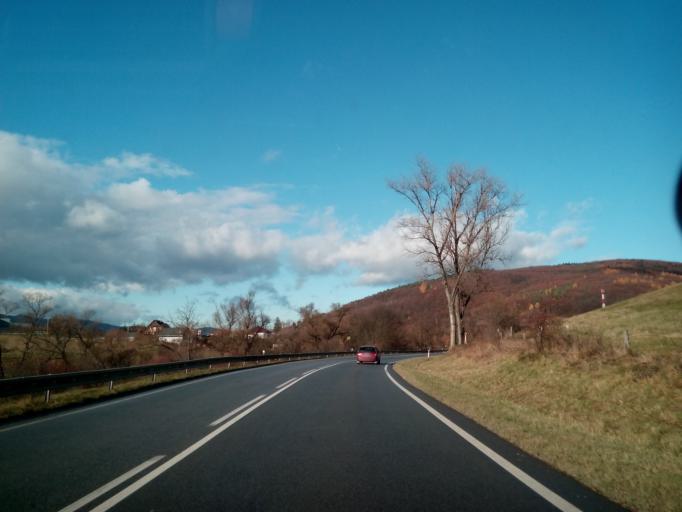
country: SK
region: Presovsky
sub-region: Okres Bardejov
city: Bardejov
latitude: 49.2527
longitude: 21.2518
